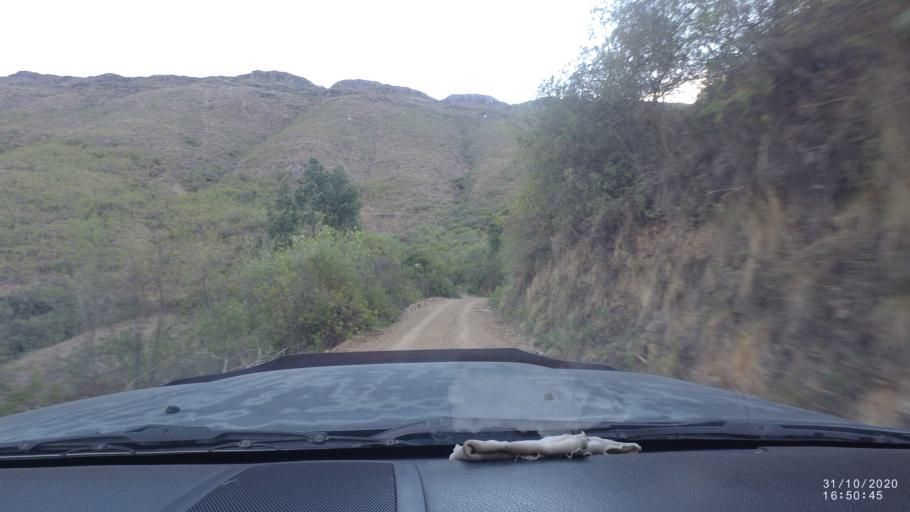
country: BO
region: Chuquisaca
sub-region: Provincia Zudanez
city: Mojocoya
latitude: -18.5099
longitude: -64.5718
